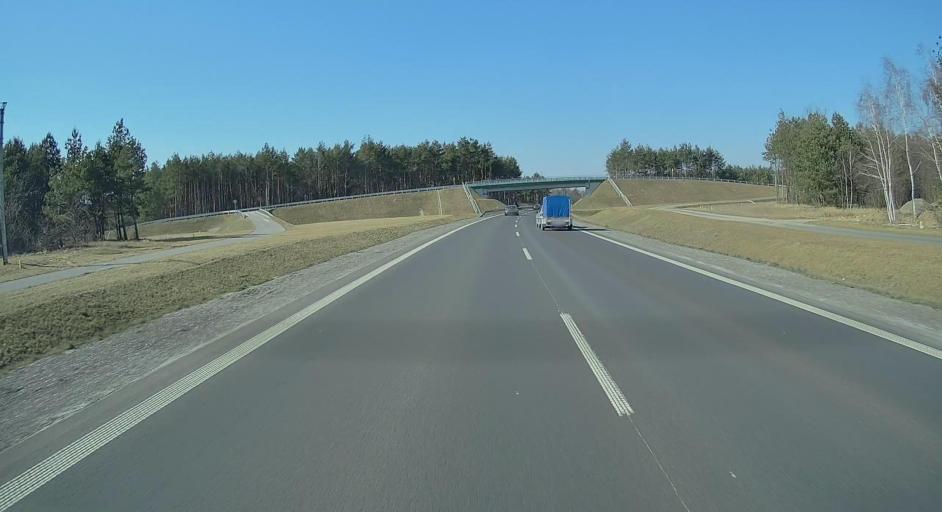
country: PL
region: Subcarpathian Voivodeship
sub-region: Powiat nizanski
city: Raclawice
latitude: 50.4957
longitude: 22.1878
